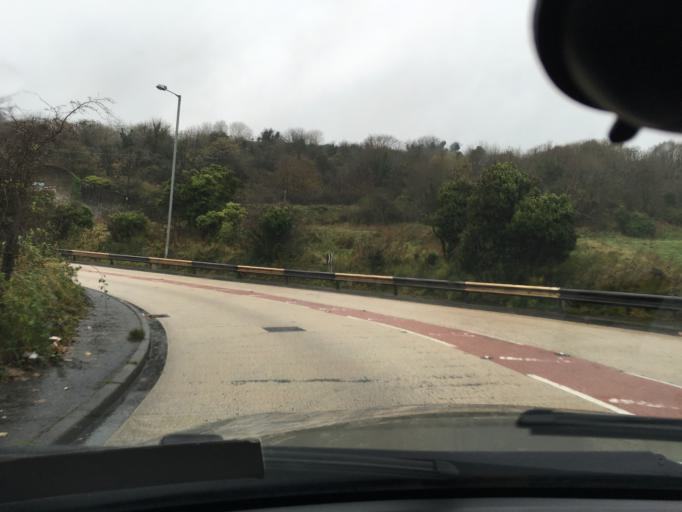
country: GB
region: Northern Ireland
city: Carnmoney
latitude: 54.6355
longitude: -5.9689
